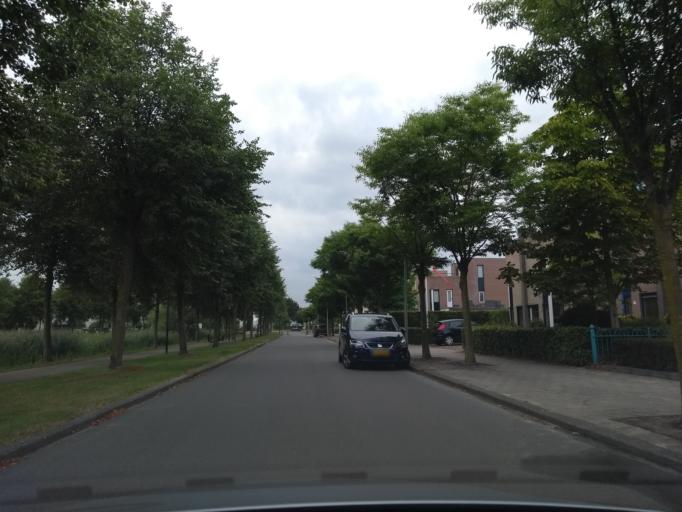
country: NL
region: Overijssel
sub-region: Gemeente Hengelo
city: Hengelo
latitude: 52.2958
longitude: 6.7972
